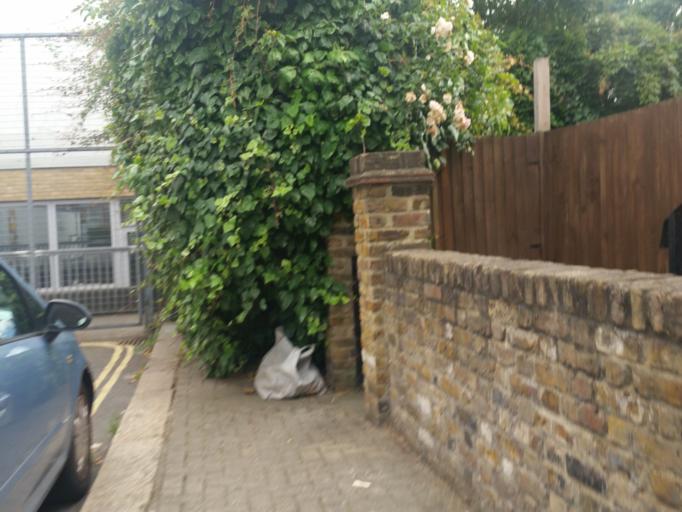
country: GB
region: England
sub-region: Greater London
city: Camden Town
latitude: 51.5457
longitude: -0.1538
